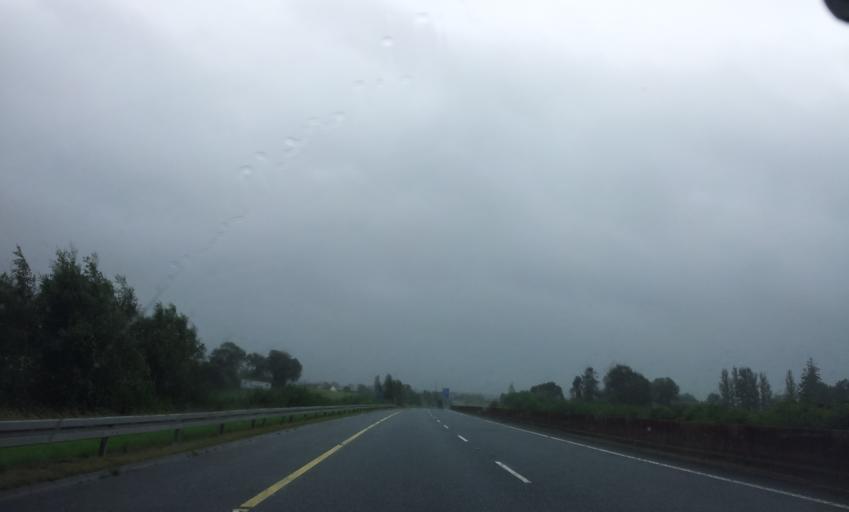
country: IE
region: Munster
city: Cahir
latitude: 52.4090
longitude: -7.9129
